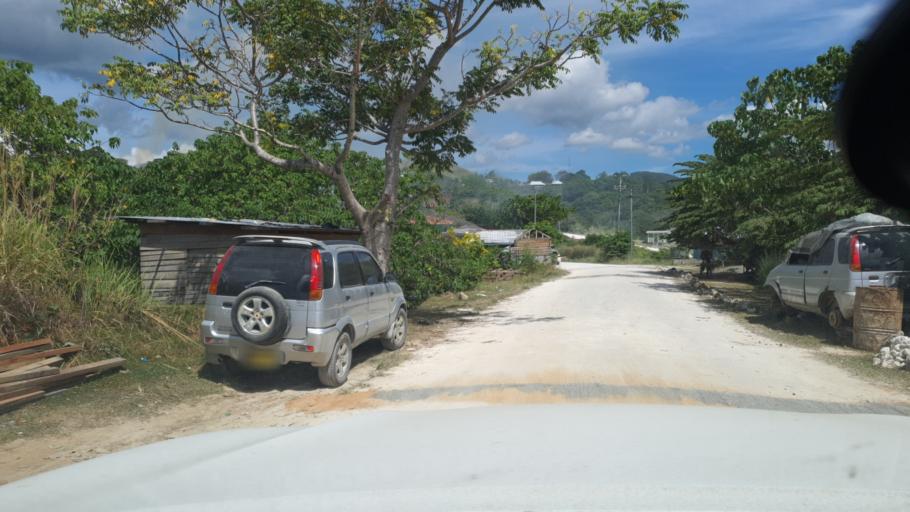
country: SB
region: Guadalcanal
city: Honiara
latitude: -9.4366
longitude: 159.9237
